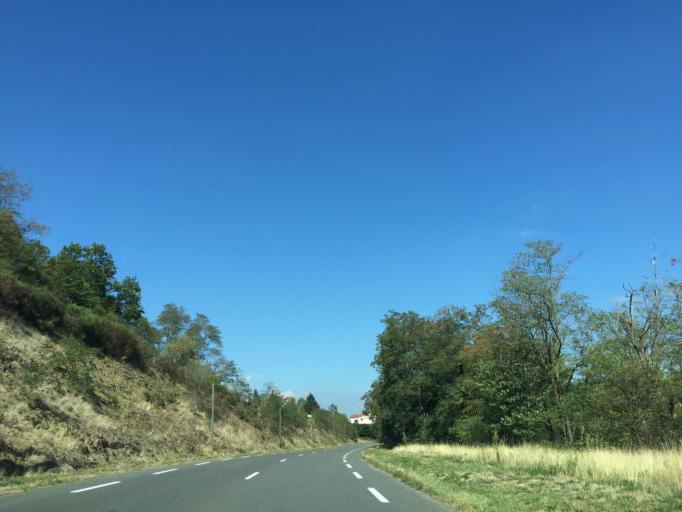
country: FR
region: Rhone-Alpes
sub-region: Departement de la Loire
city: Saint-Paul-en-Jarez
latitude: 45.4606
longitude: 4.5826
